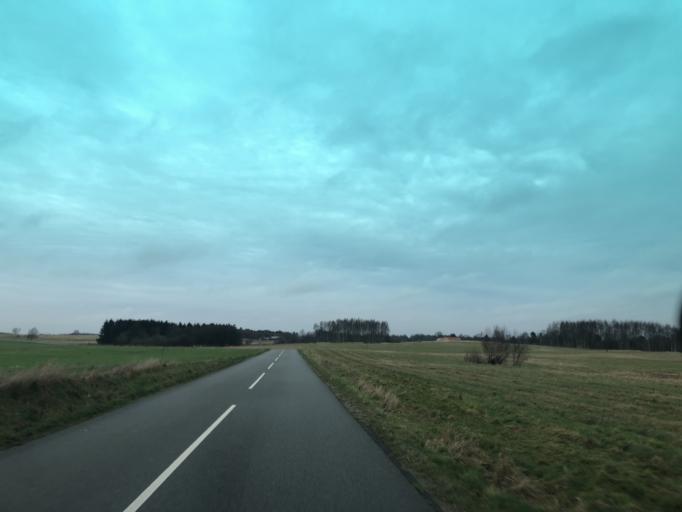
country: DK
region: Capital Region
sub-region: Frederikssund Kommune
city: Slangerup
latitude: 55.8608
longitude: 12.2293
